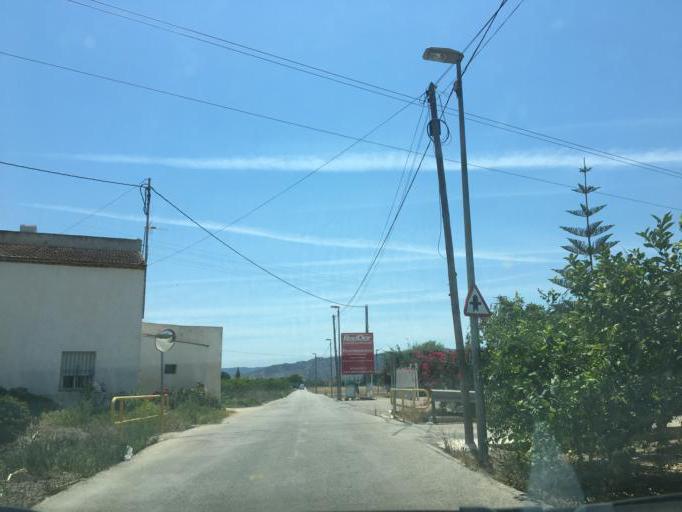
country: ES
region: Murcia
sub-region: Murcia
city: Santomera
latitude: 38.0291
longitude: -1.0629
